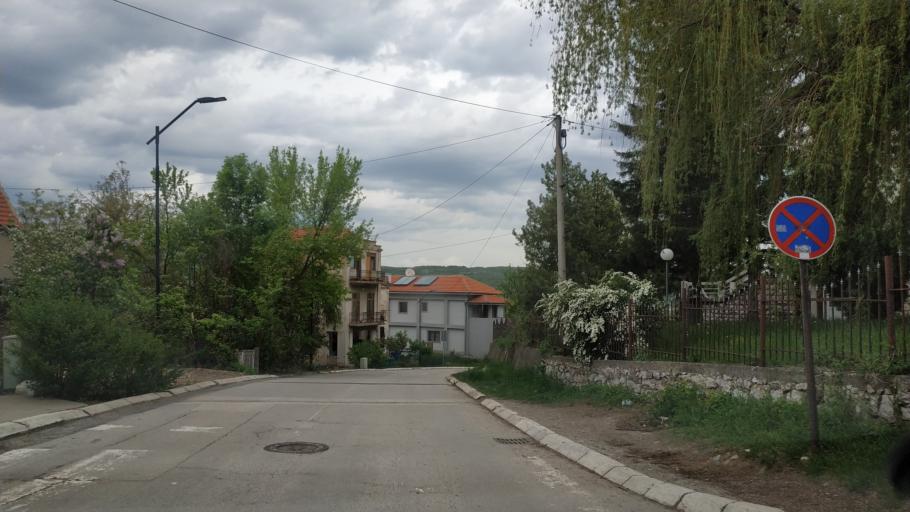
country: RS
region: Central Serbia
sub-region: Zajecarski Okrug
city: Soko Banja
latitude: 43.6411
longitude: 21.8707
